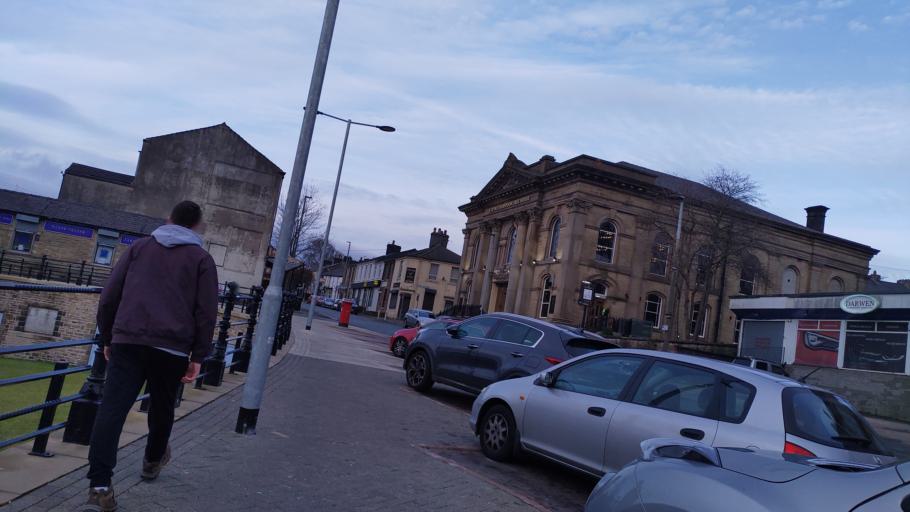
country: GB
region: England
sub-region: Blackburn with Darwen
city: Darwen
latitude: 53.6955
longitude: -2.4659
